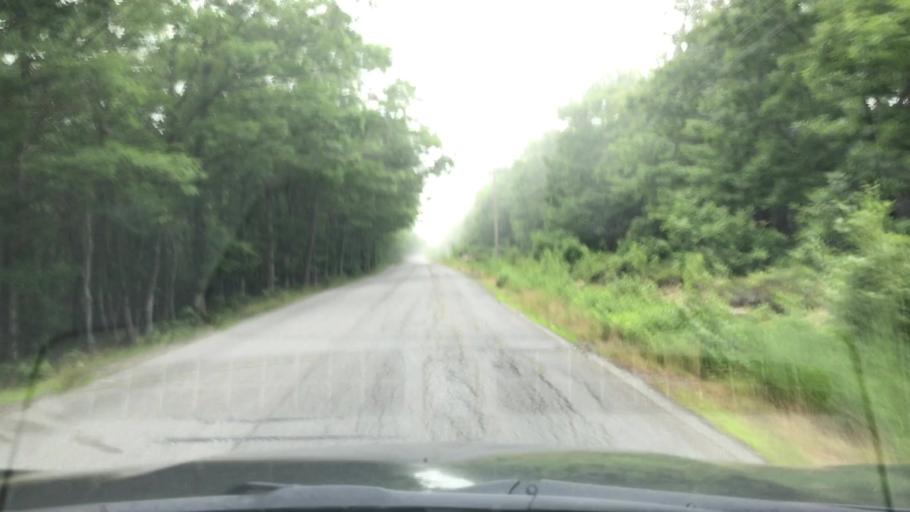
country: US
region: Maine
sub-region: Hancock County
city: Bar Harbor
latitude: 44.3502
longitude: -68.1825
